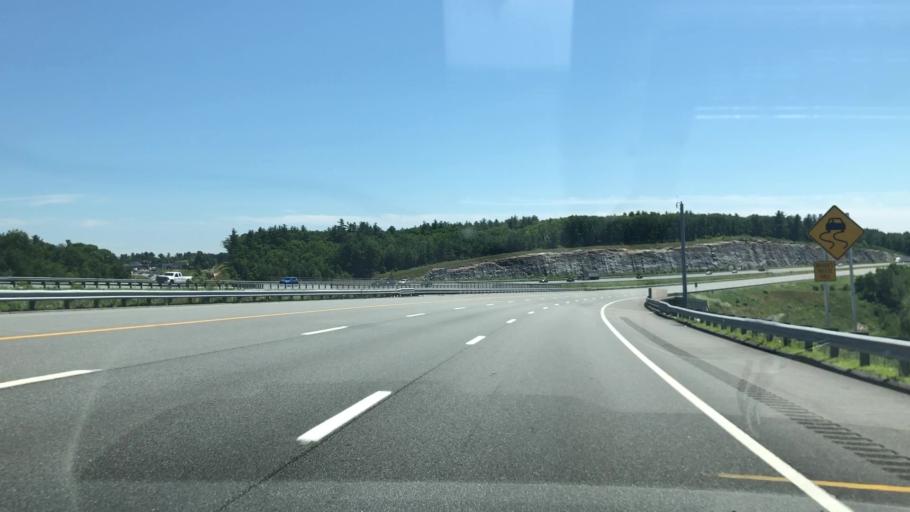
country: US
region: New Hampshire
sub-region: Rockingham County
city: Windham
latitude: 42.8102
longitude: -71.2738
